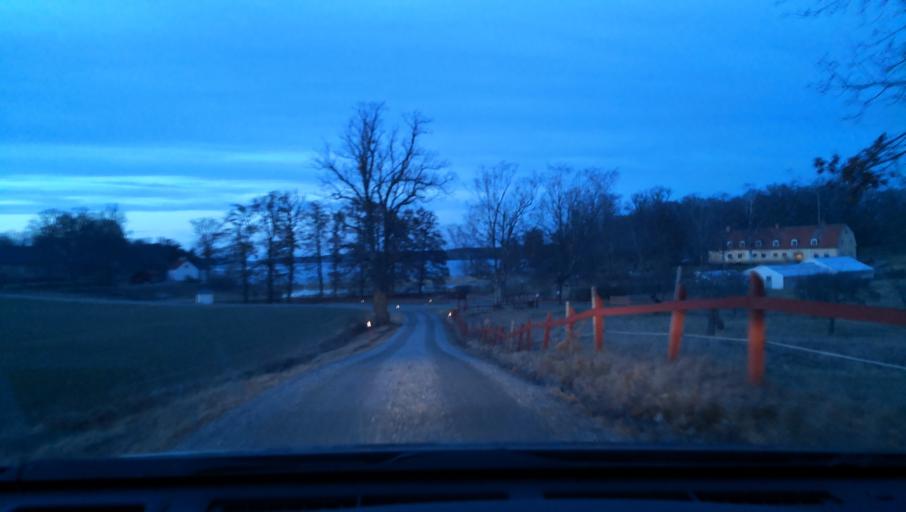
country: SE
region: Uppsala
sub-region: Enkopings Kommun
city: Dalby
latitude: 59.5723
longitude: 17.3792
